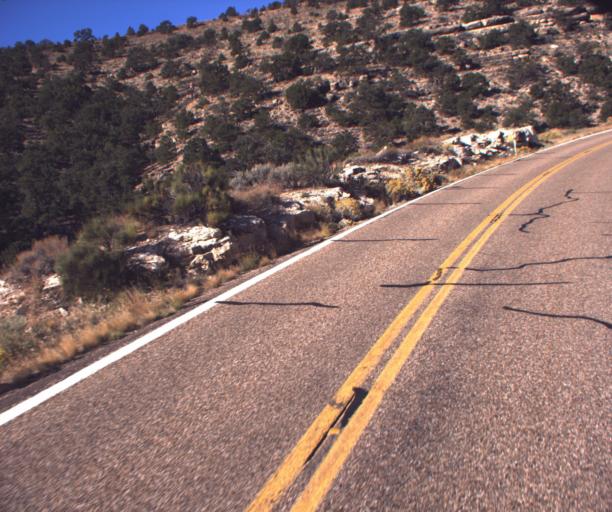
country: US
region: Arizona
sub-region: Coconino County
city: Fredonia
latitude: 36.7246
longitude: -112.0808
